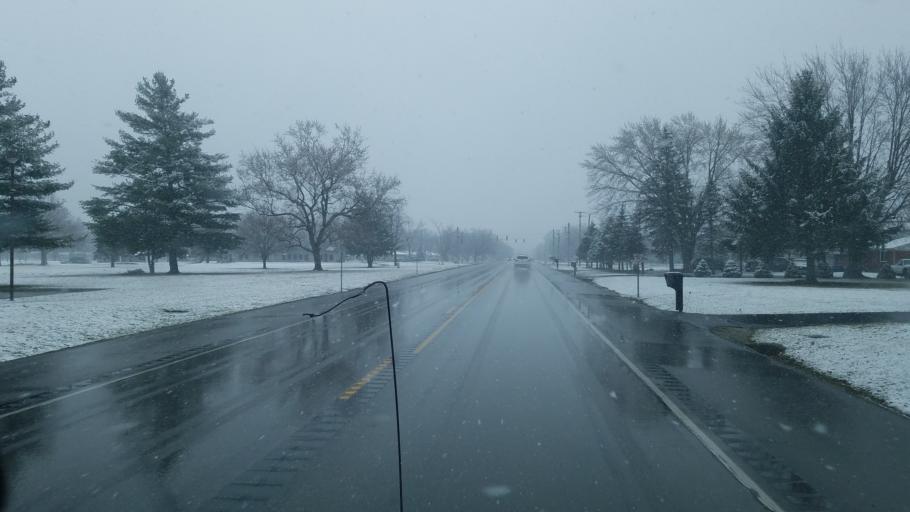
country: US
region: Indiana
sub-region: Grant County
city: Marion
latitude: 40.5833
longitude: -85.6810
